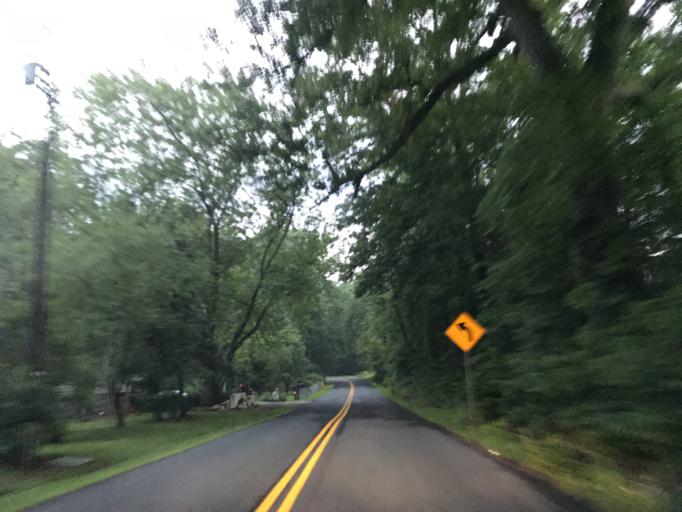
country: US
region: Maryland
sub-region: Harford County
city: Fallston
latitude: 39.4942
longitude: -76.4179
